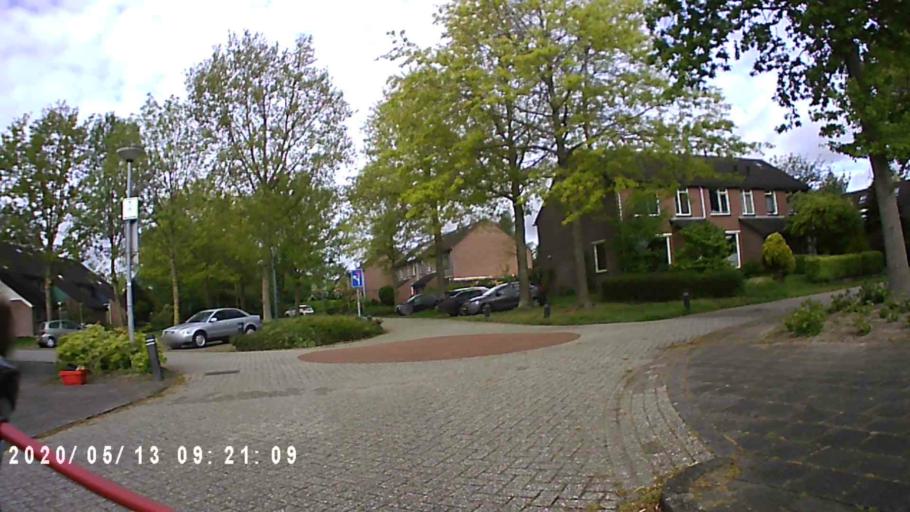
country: NL
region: Groningen
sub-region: Gemeente Zuidhorn
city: Noordhorn
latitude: 53.2638
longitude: 6.3996
